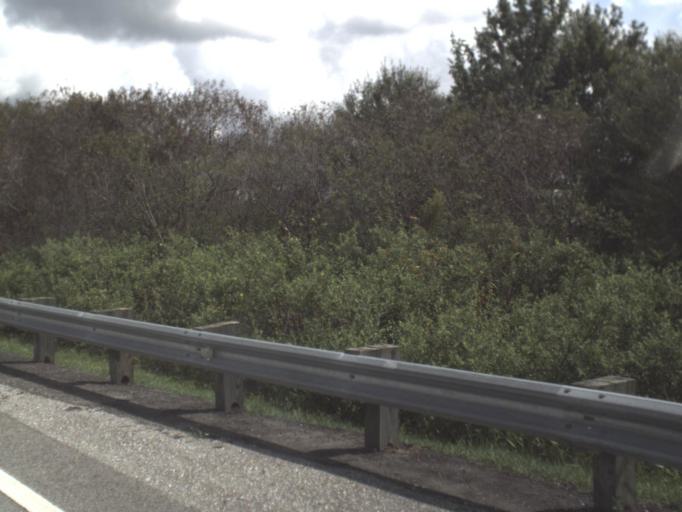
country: US
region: Florida
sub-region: Sarasota County
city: Warm Mineral Springs
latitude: 27.2007
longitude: -82.2342
